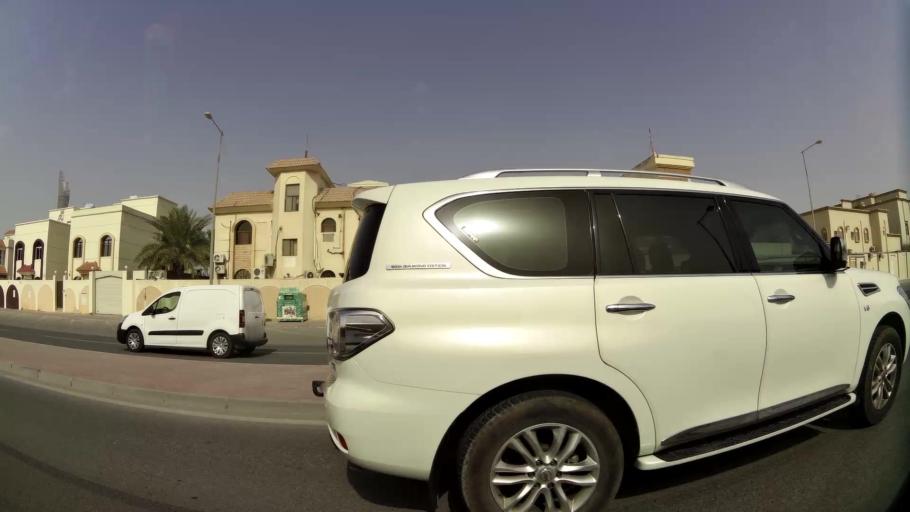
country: QA
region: Baladiyat ar Rayyan
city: Ar Rayyan
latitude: 25.2530
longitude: 51.4412
